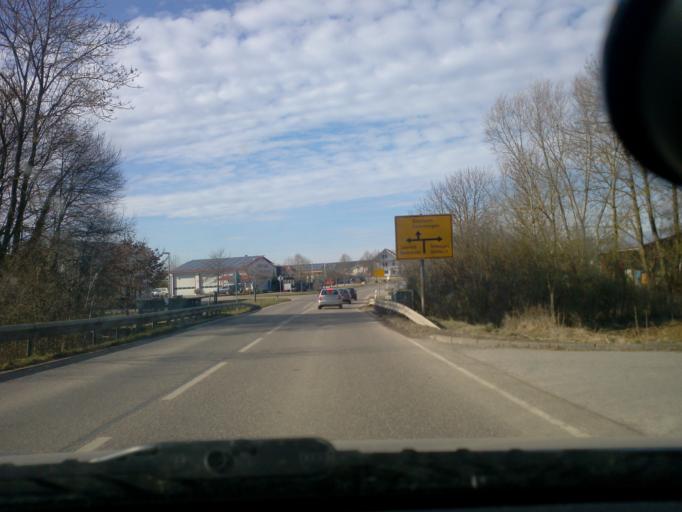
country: DE
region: Baden-Wuerttemberg
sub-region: Regierungsbezirk Stuttgart
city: Gemmingen
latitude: 49.1264
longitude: 9.0078
